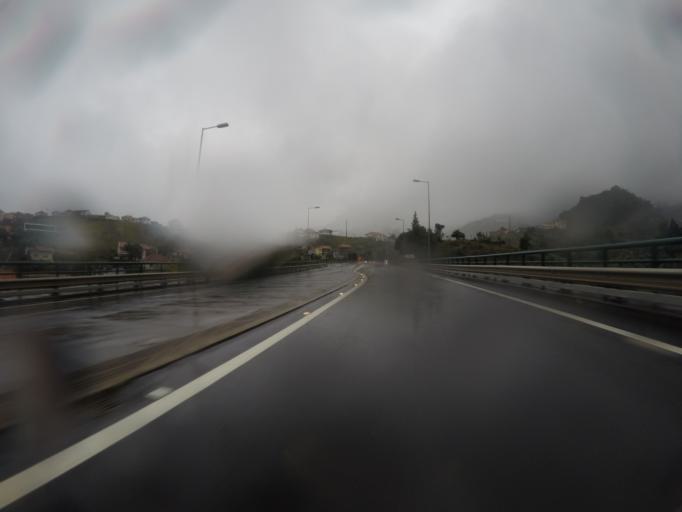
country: PT
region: Madeira
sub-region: Santana
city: Santana
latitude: 32.7618
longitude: -16.8304
